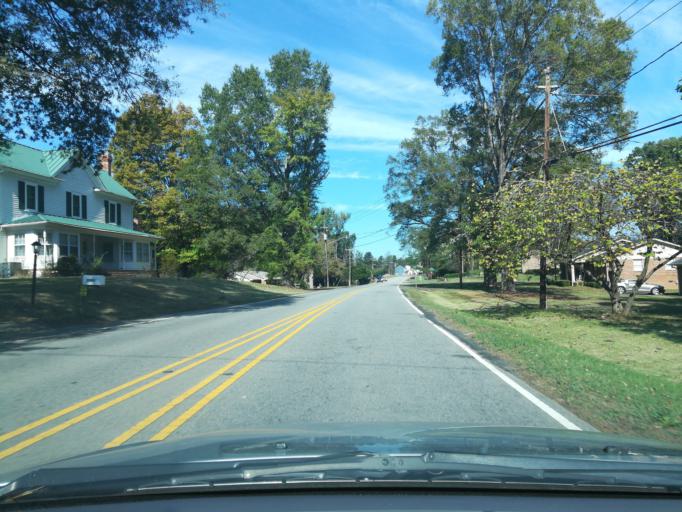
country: US
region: North Carolina
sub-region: Durham County
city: Durham
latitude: 35.9677
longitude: -78.9767
